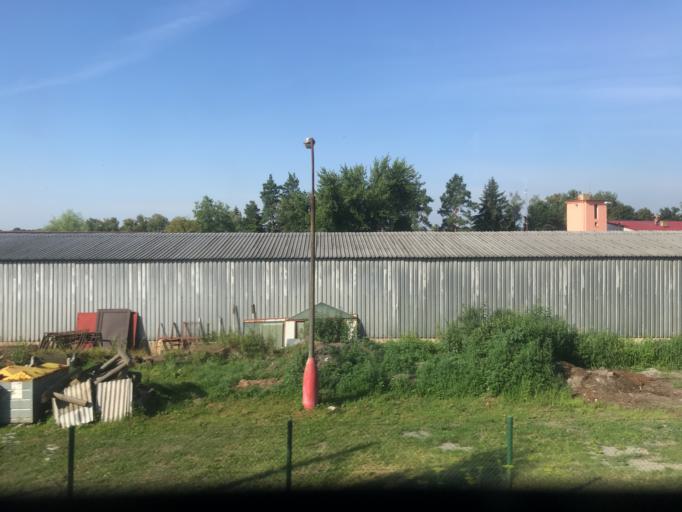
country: CZ
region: Jihocesky
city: Sobeslav
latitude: 49.2631
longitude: 14.7242
